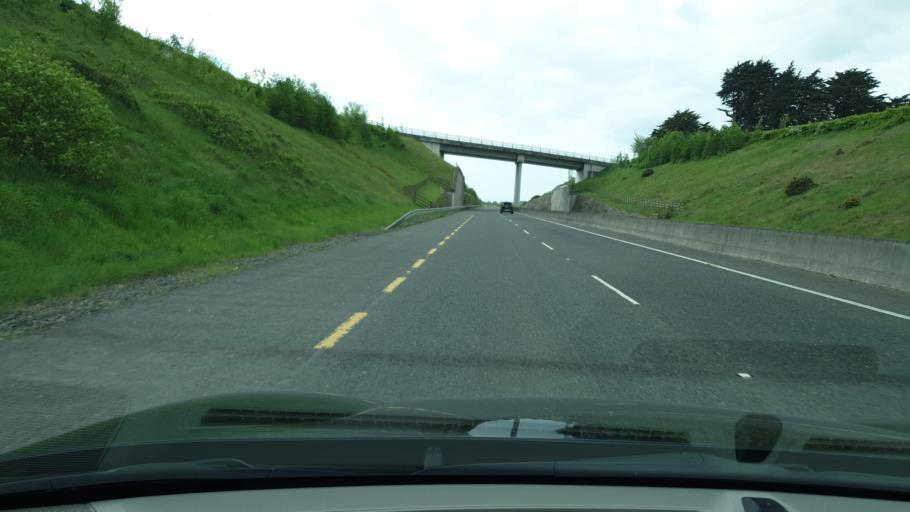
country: IE
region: Leinster
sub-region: An Mhi
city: Navan
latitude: 53.6314
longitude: -6.6683
